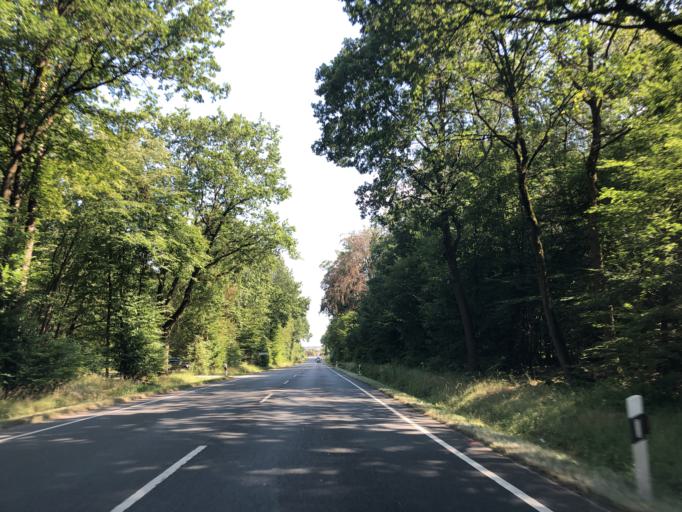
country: DE
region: Hesse
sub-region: Regierungsbezirk Darmstadt
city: Dietzenbach
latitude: 50.0272
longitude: 8.7685
